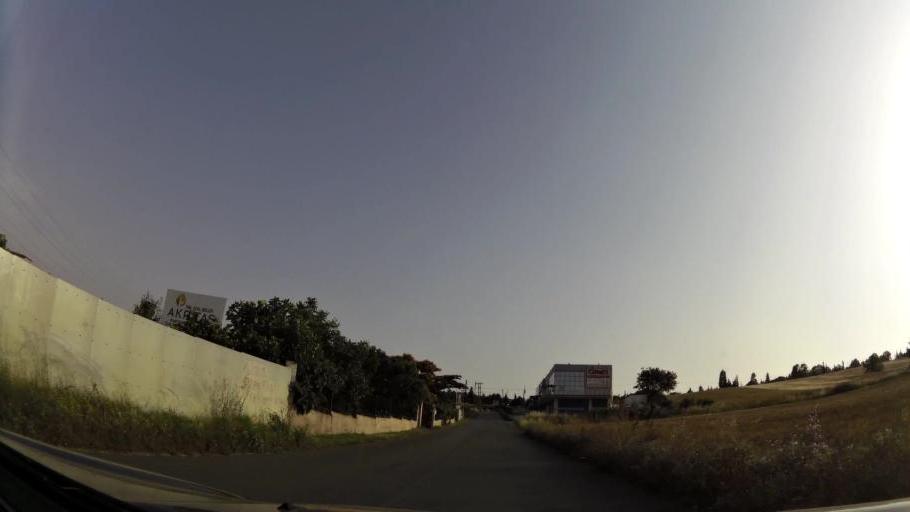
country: GR
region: Central Macedonia
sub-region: Nomos Thessalonikis
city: Evosmos
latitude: 40.6924
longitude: 22.9069
